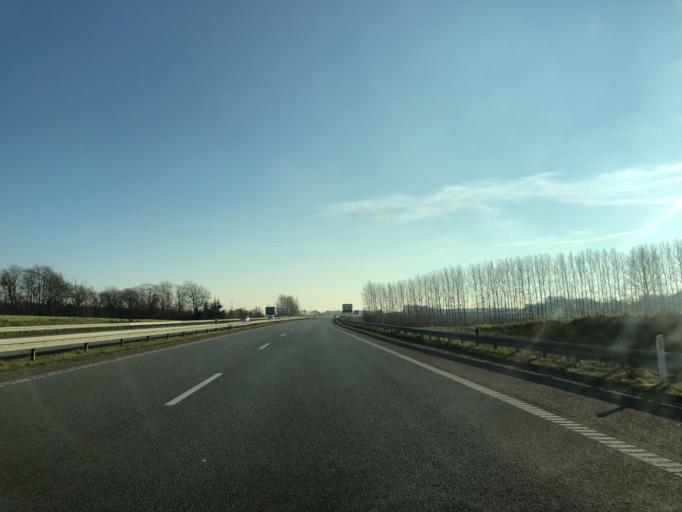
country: DK
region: South Denmark
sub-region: Vejle Kommune
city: Give
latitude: 55.8629
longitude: 9.2598
